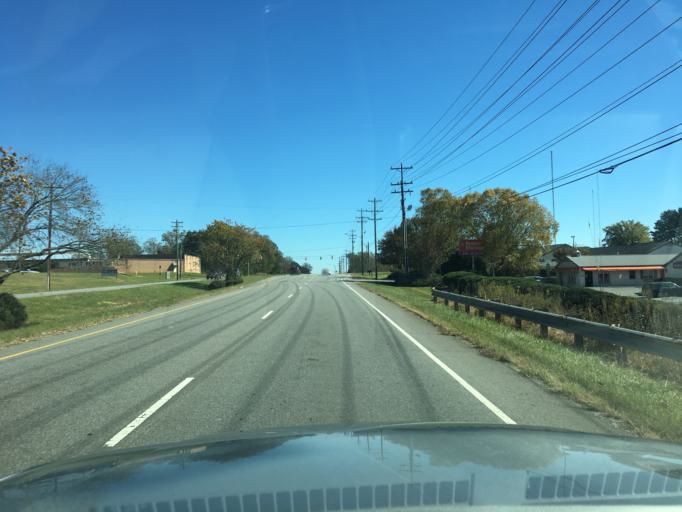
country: US
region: North Carolina
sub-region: Catawba County
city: Hickory
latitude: 35.7282
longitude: -81.3043
